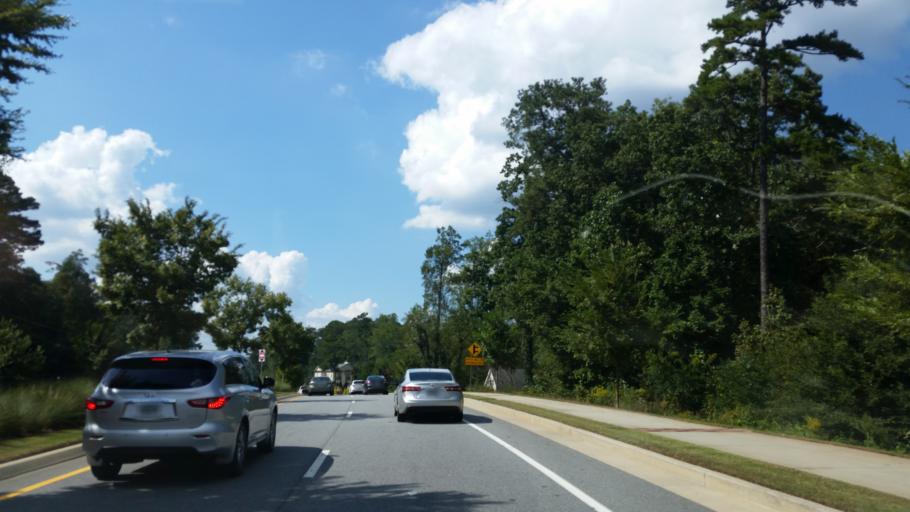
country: US
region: Georgia
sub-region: Fulton County
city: Sandy Springs
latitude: 33.9388
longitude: -84.3955
